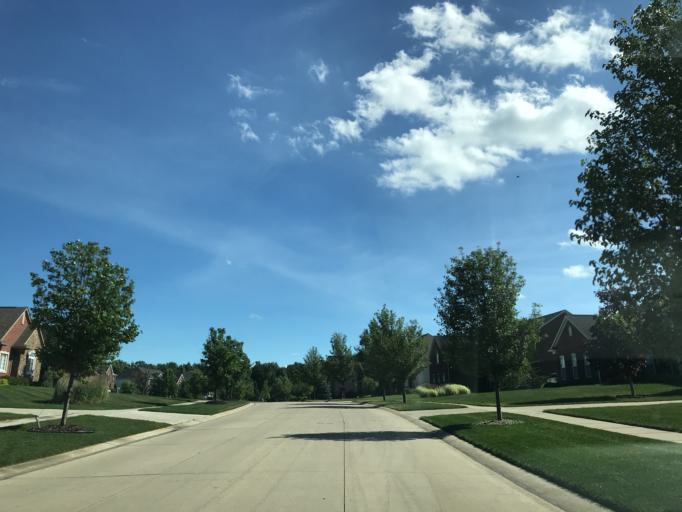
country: US
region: Michigan
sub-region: Oakland County
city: Wixom
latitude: 42.4613
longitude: -83.5668
